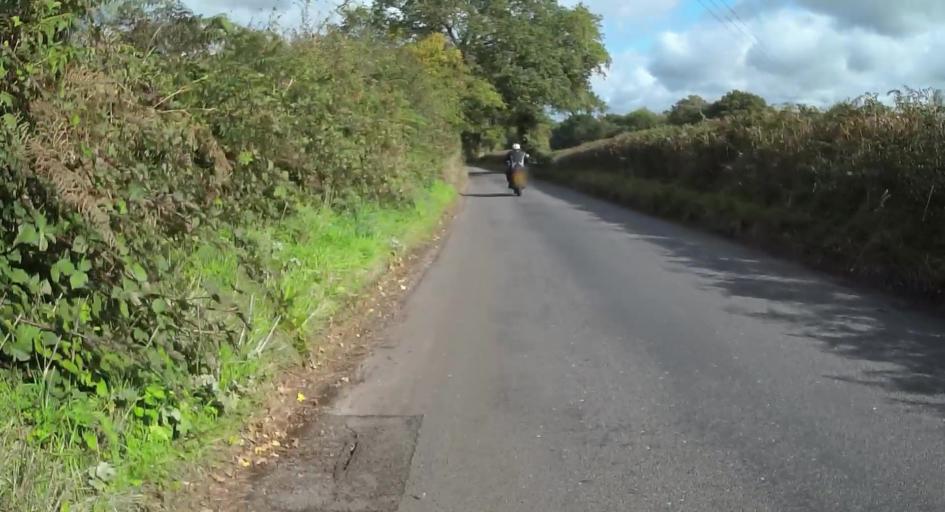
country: GB
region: England
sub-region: Hampshire
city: Fleet
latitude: 51.2833
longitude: -0.8791
